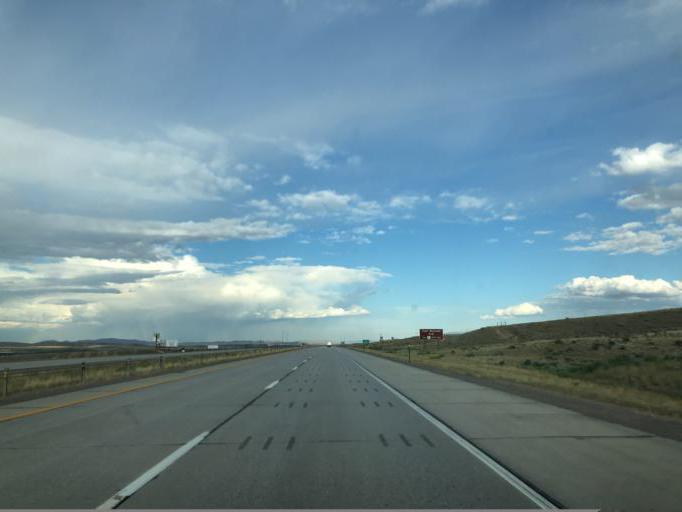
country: US
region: Wyoming
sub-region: Carbon County
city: Rawlins
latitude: 41.7780
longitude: -107.2398
